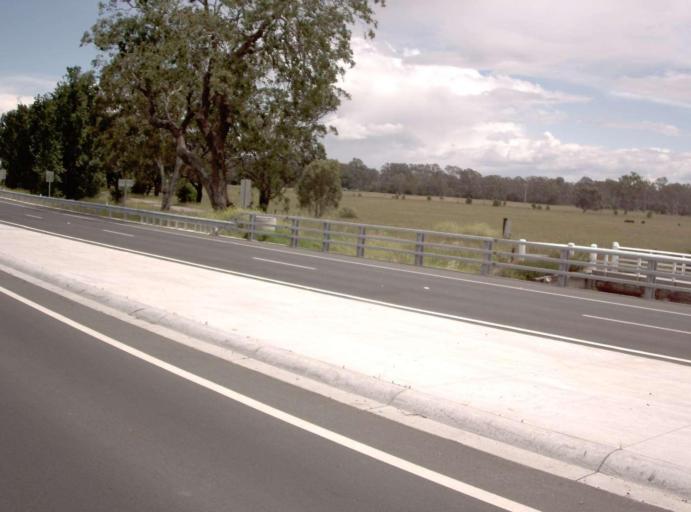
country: AU
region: Victoria
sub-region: Wellington
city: Sale
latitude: -38.1127
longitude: 147.0553
